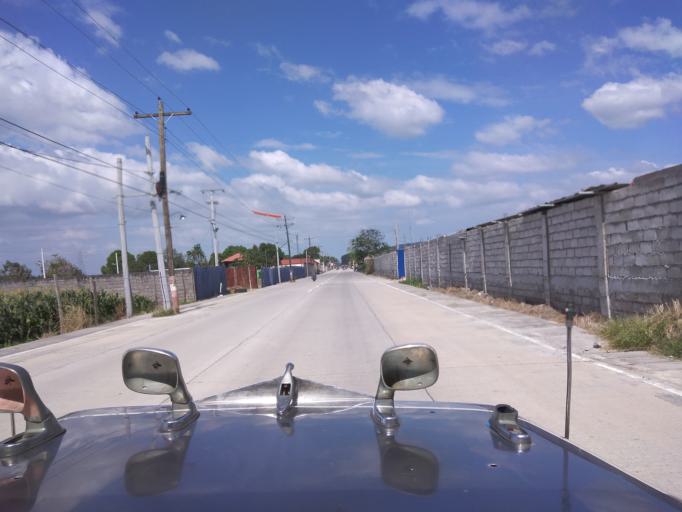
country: PH
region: Central Luzon
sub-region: Province of Pampanga
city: Anao
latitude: 15.1344
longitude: 120.6958
